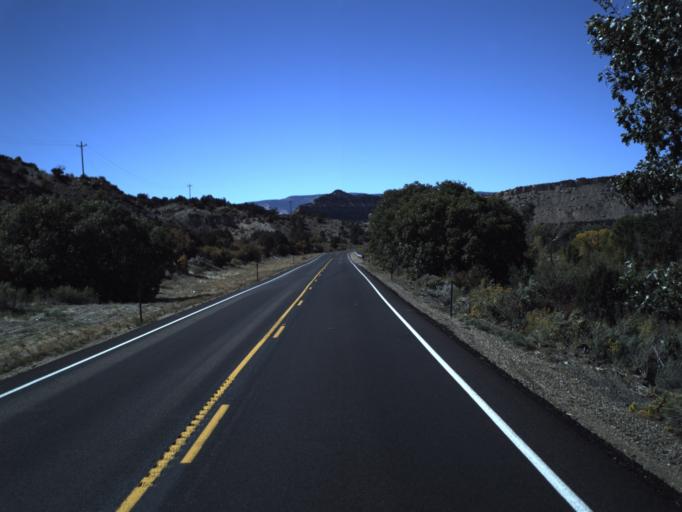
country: US
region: Utah
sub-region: Wayne County
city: Loa
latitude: 37.7723
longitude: -111.6517
